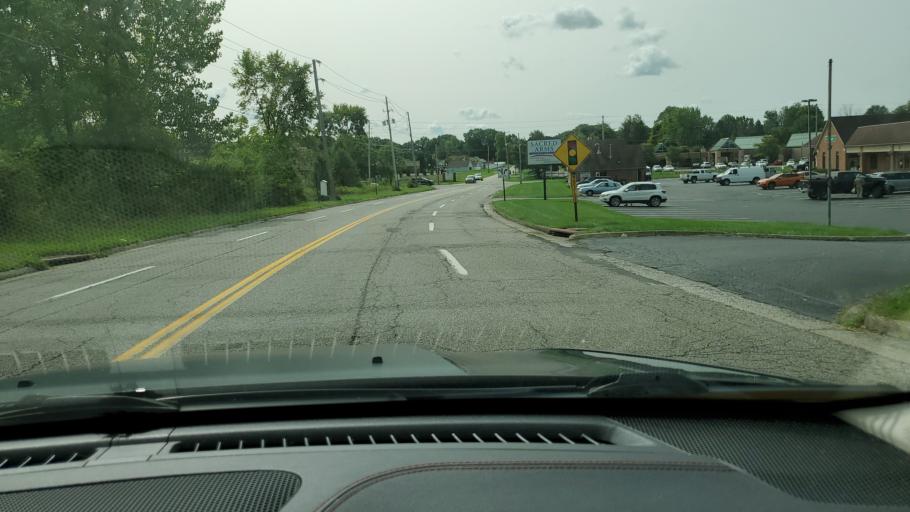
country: US
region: Ohio
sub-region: Mahoning County
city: Boardman
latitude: 40.9893
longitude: -80.6693
